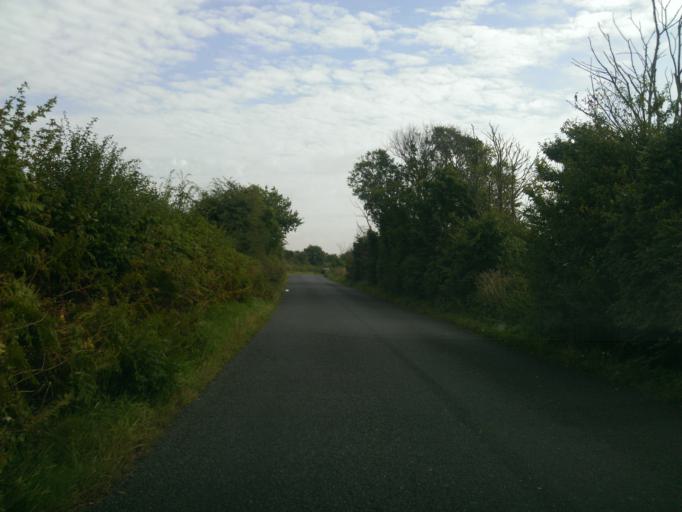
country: GB
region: England
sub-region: Essex
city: Saint Osyth
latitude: 51.8059
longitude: 1.0861
